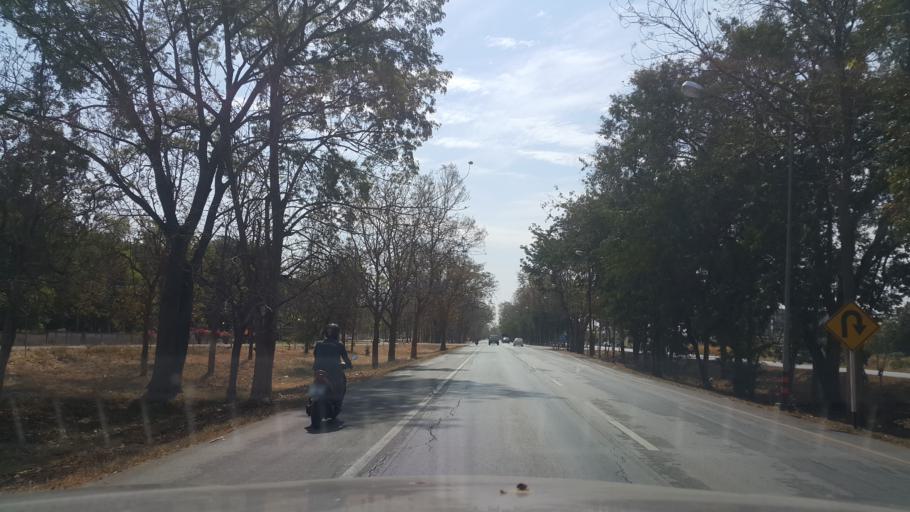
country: TH
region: Nakhon Ratchasima
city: Nakhon Ratchasima
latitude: 14.8755
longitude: 102.0723
